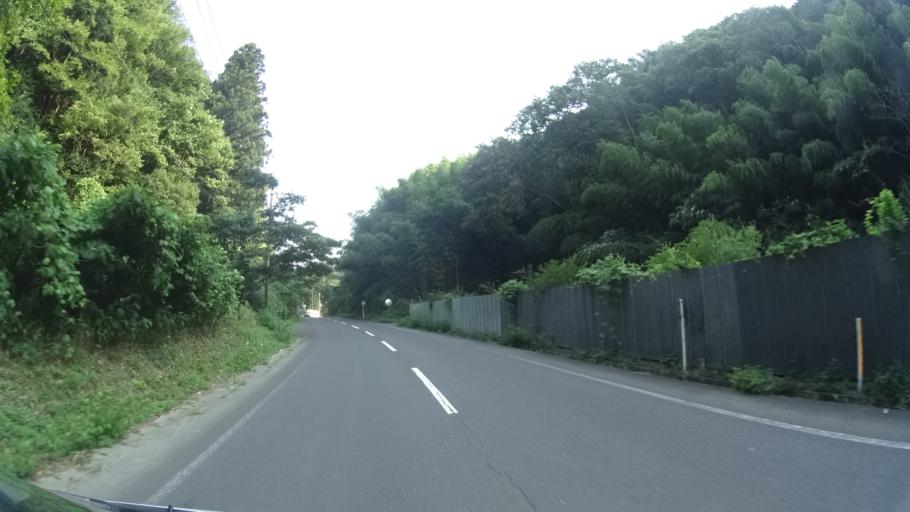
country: JP
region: Kyoto
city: Maizuru
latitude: 35.4515
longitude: 135.2821
